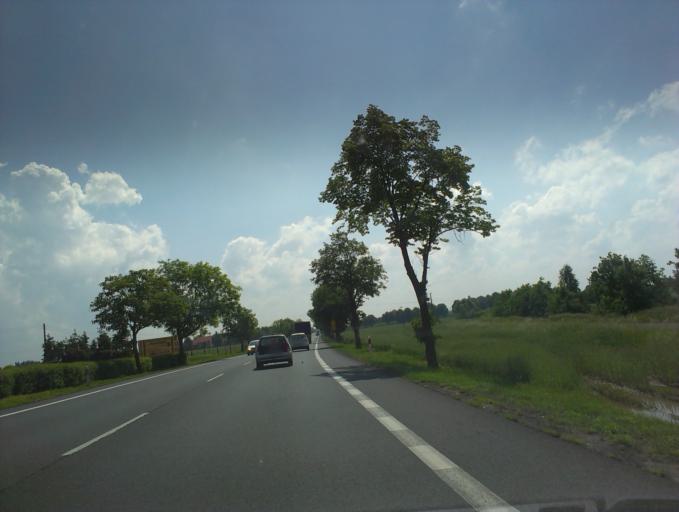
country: PL
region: Greater Poland Voivodeship
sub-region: Powiat pilski
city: Ujscie
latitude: 53.0429
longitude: 16.7608
